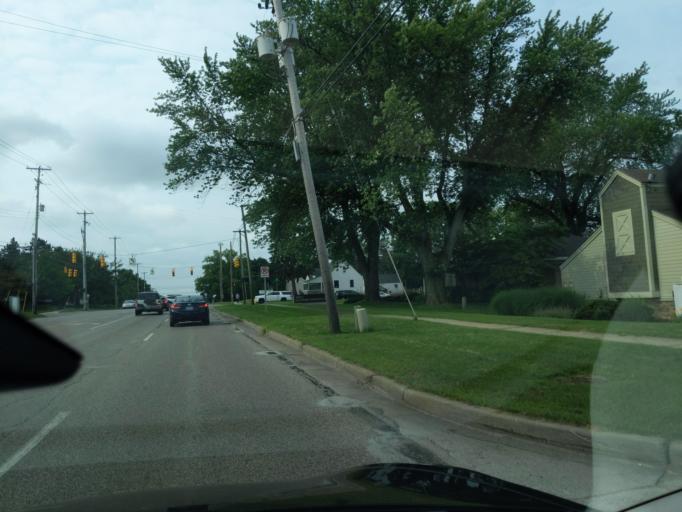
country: US
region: Michigan
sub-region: Kent County
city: East Grand Rapids
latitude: 42.9113
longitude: -85.5687
